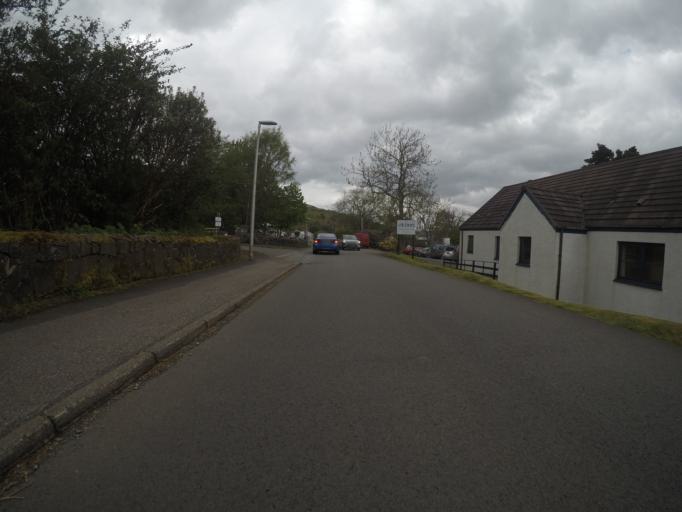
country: GB
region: Scotland
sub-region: Highland
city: Isle of Skye
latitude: 57.3013
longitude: -6.3523
